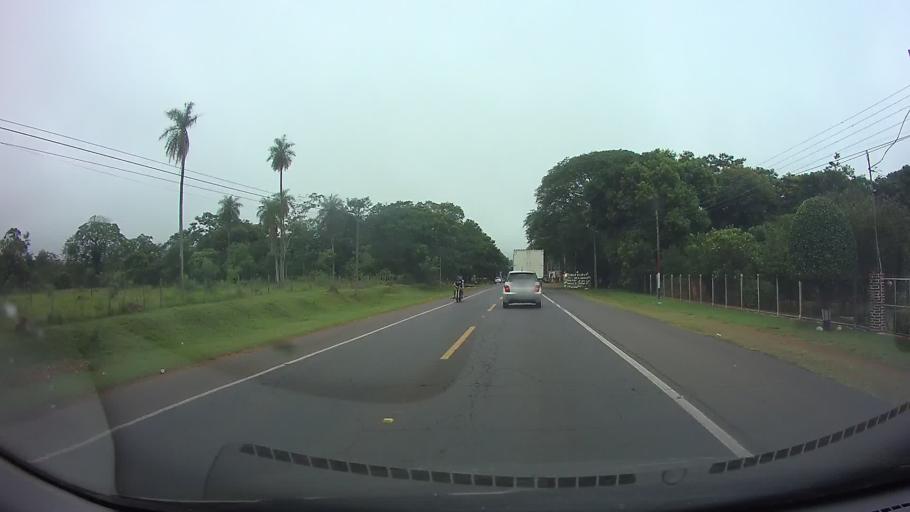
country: PY
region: Paraguari
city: Paraguari
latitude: -25.6011
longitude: -57.1956
